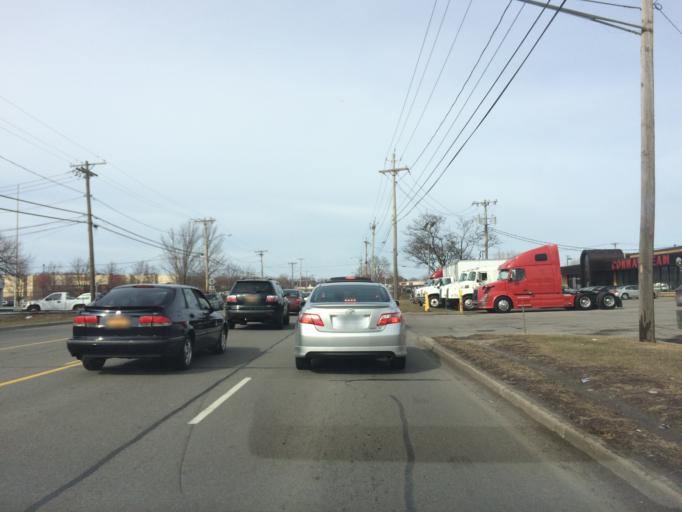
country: US
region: New York
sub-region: Monroe County
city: Rochester
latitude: 43.0981
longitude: -77.6309
